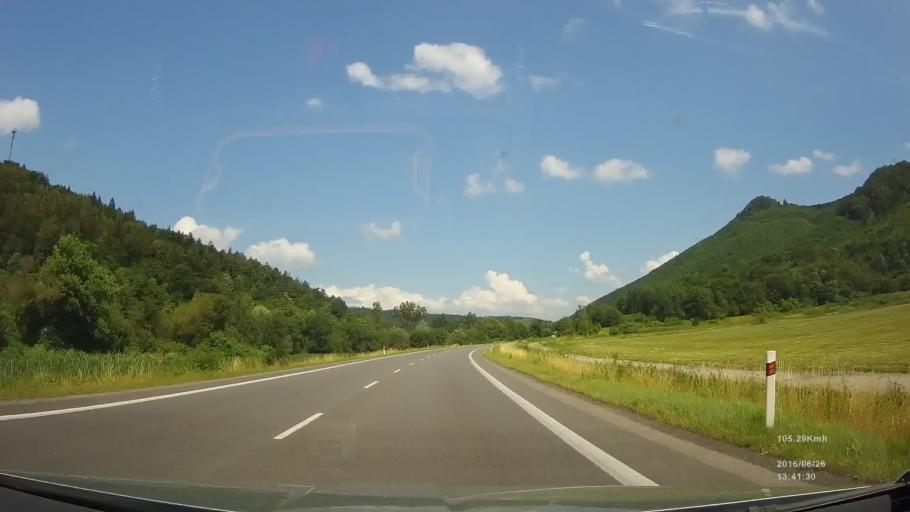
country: SK
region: Banskobystricky
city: Hrochot,Slovakia
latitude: 48.7727
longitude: 19.2967
